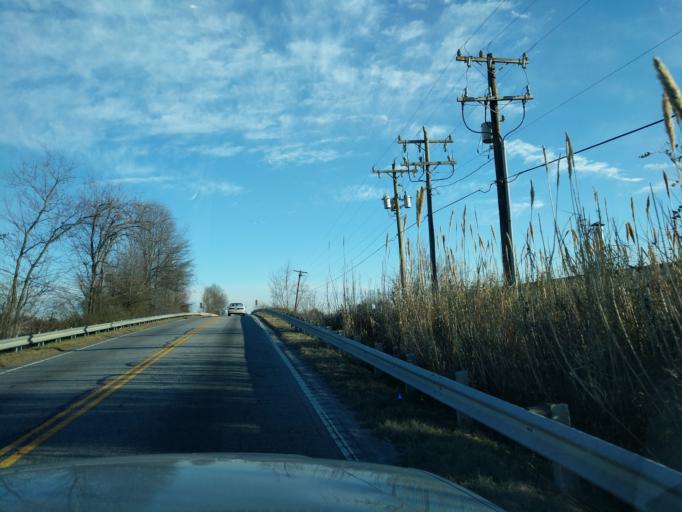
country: US
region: South Carolina
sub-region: Anderson County
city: Williamston
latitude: 34.6671
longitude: -82.5178
